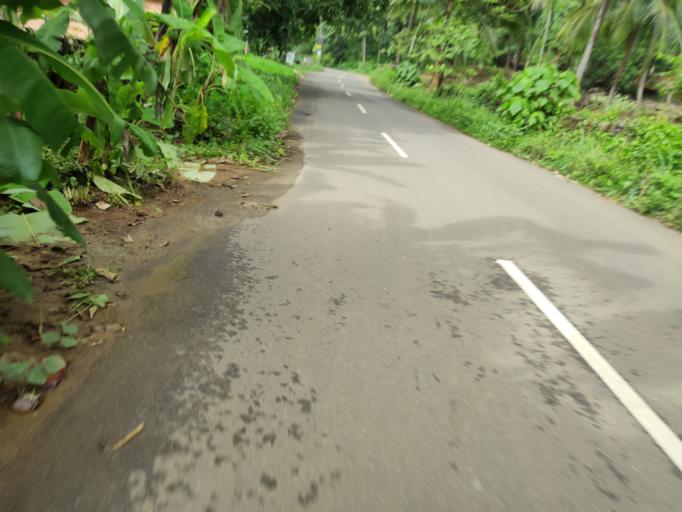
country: IN
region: Kerala
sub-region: Malappuram
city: Manjeri
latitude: 11.1383
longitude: 76.1308
